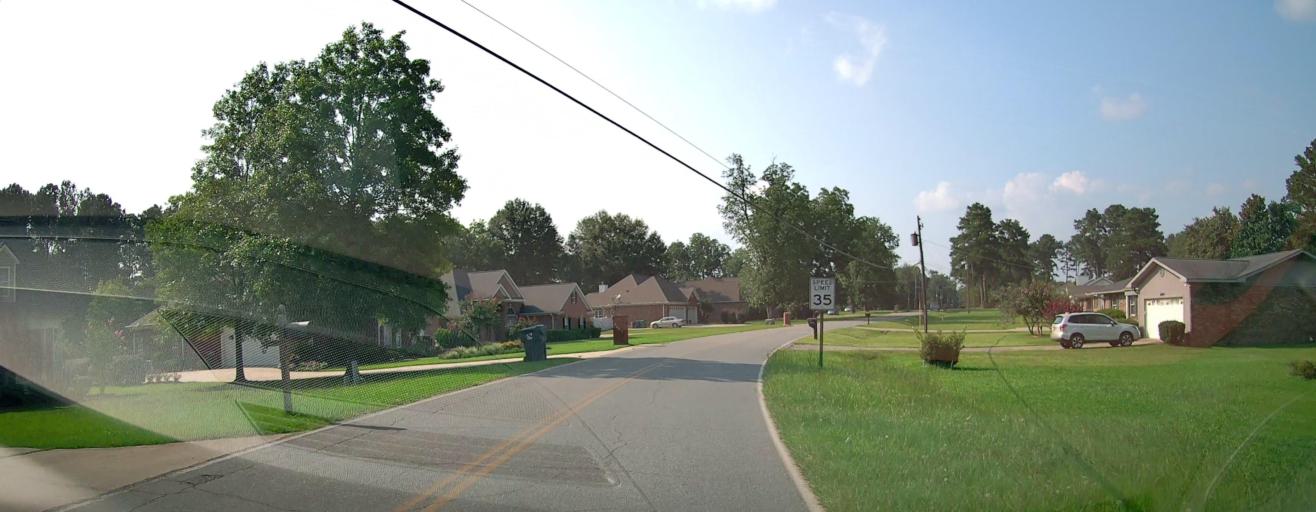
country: US
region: Georgia
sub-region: Houston County
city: Centerville
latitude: 32.7251
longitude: -83.6890
